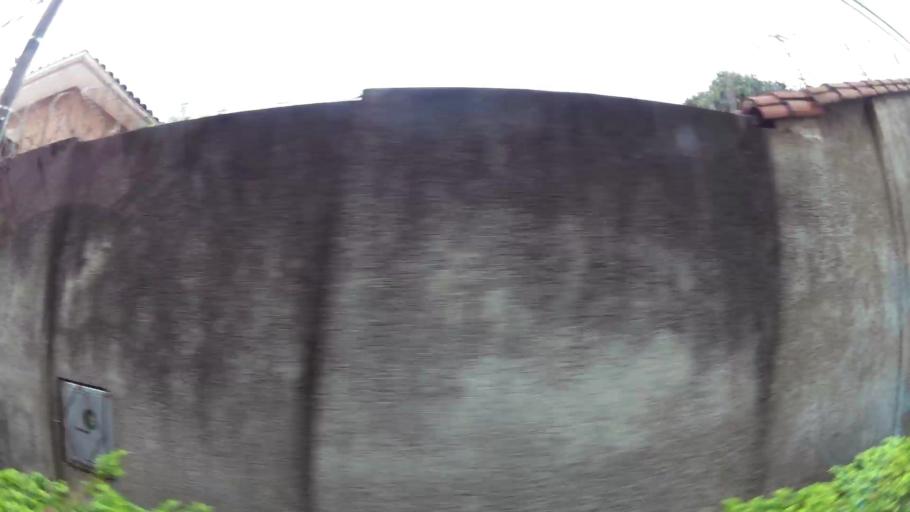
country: BO
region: Santa Cruz
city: Santa Cruz de la Sierra
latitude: -17.7727
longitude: -63.1580
